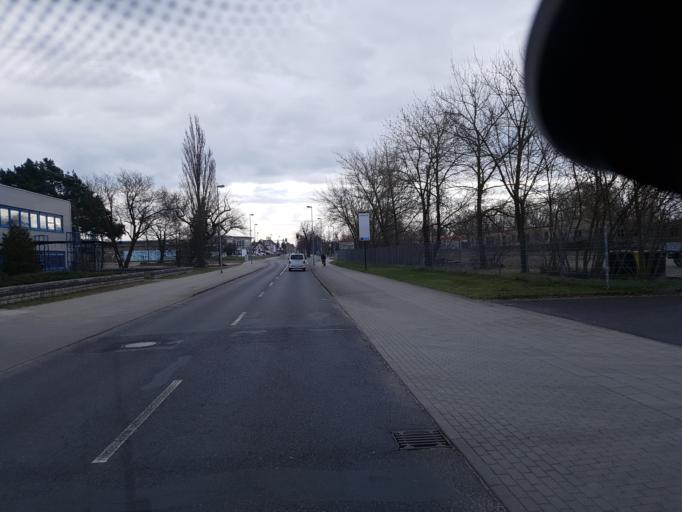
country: DE
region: Brandenburg
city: Eisenhuettenstadt
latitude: 52.1487
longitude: 14.6496
